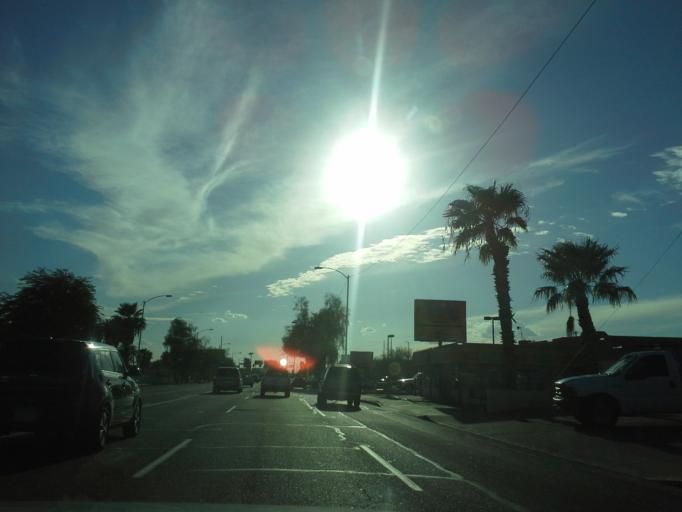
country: US
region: Arizona
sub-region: Maricopa County
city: Phoenix
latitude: 33.4512
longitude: -112.1139
